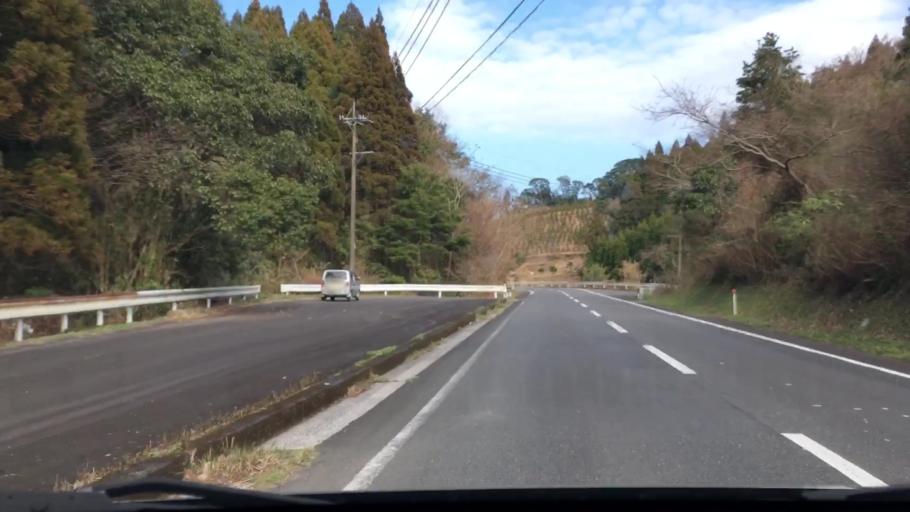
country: JP
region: Miyazaki
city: Kushima
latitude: 31.5711
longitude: 131.2632
